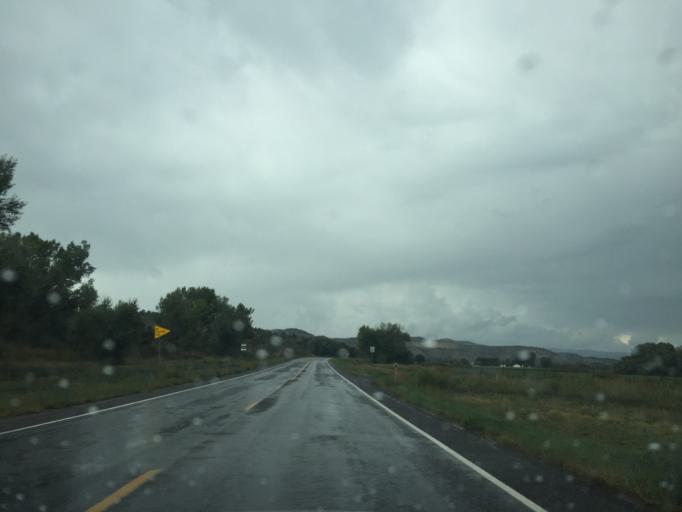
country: US
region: Utah
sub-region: Kane County
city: Kanab
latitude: 37.2545
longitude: -112.6598
